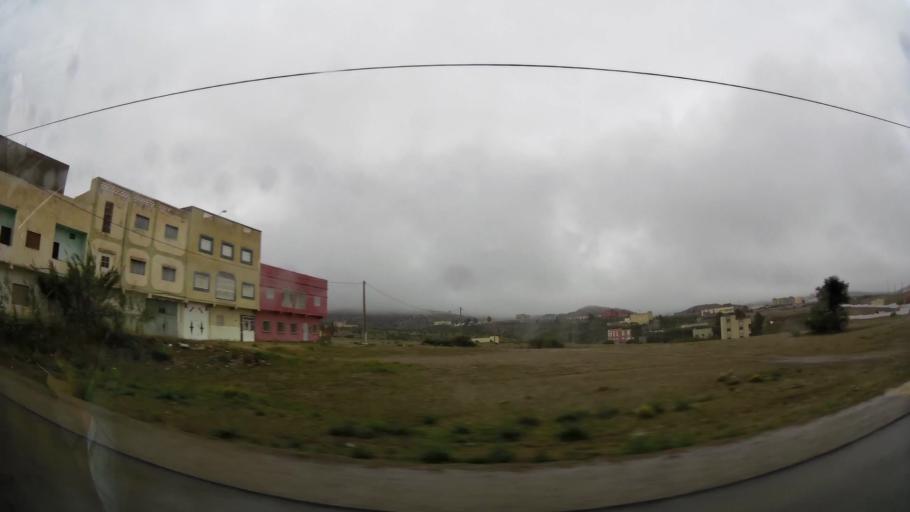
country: MA
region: Taza-Al Hoceima-Taounate
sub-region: Taza
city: Aknoul
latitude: 34.8169
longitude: -3.7292
